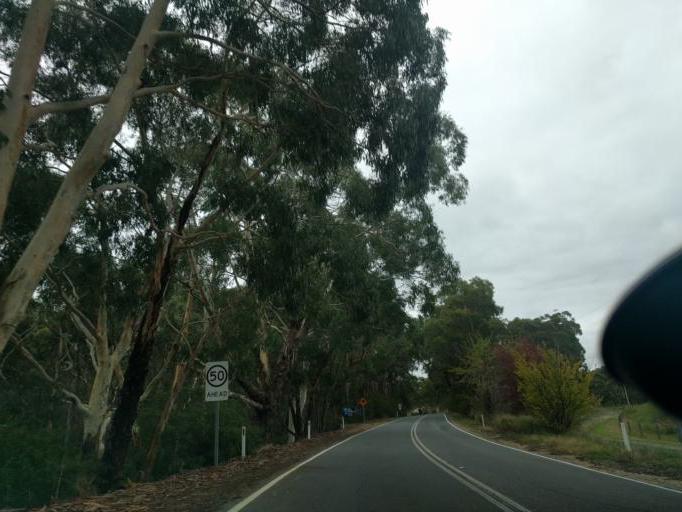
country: AU
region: South Australia
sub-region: Adelaide Hills
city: Stirling
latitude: -35.0484
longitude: 138.7587
